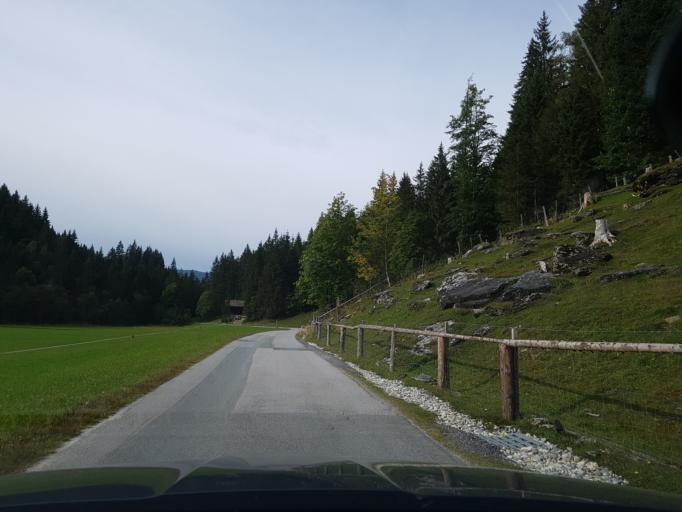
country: AT
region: Salzburg
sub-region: Politischer Bezirk Sankt Johann im Pongau
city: Forstau
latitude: 47.3523
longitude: 13.5720
